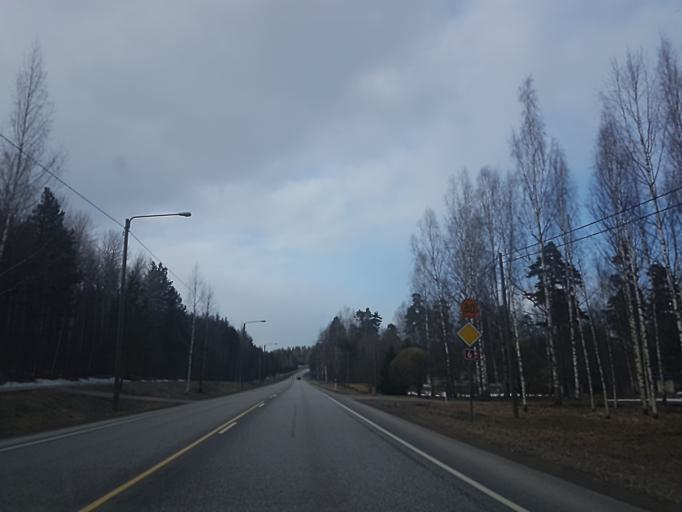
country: FI
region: South Karelia
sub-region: Imatra
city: Parikkala
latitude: 61.5318
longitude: 29.5171
